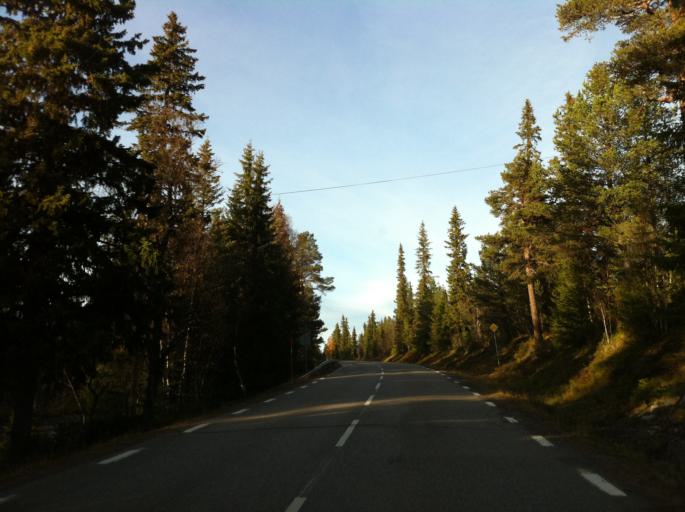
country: NO
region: Hedmark
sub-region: Engerdal
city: Engerdal
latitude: 62.0691
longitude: 12.3138
